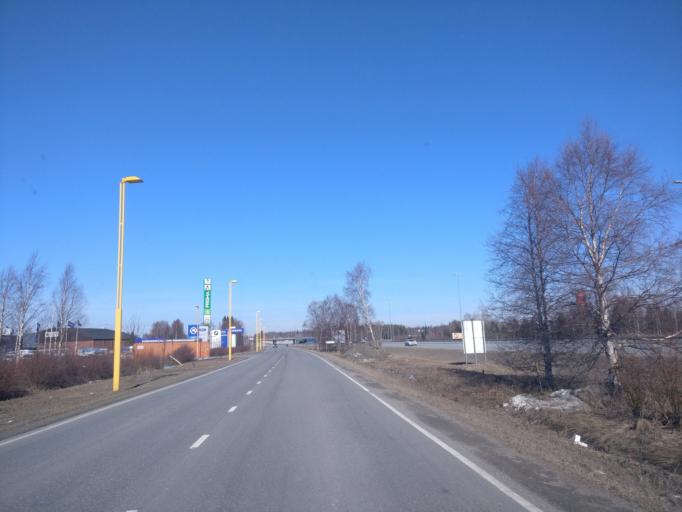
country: FI
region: Lapland
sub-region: Kemi-Tornio
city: Kemi
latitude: 65.7395
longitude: 24.5867
